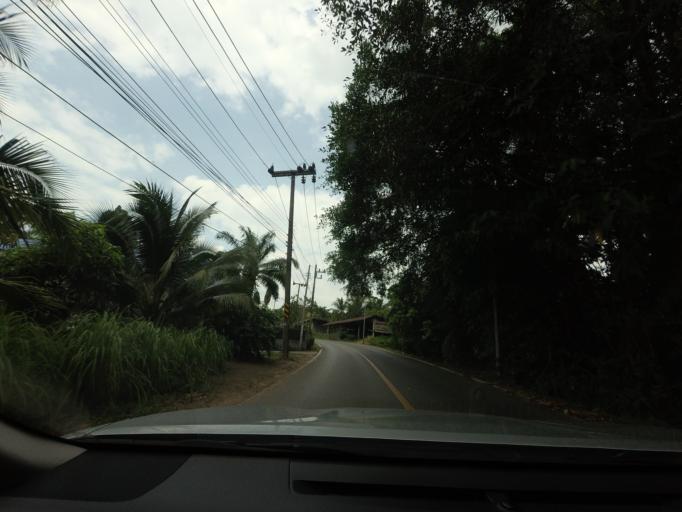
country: TH
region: Phangnga
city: Ban Ao Nang
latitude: 8.0829
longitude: 98.7457
